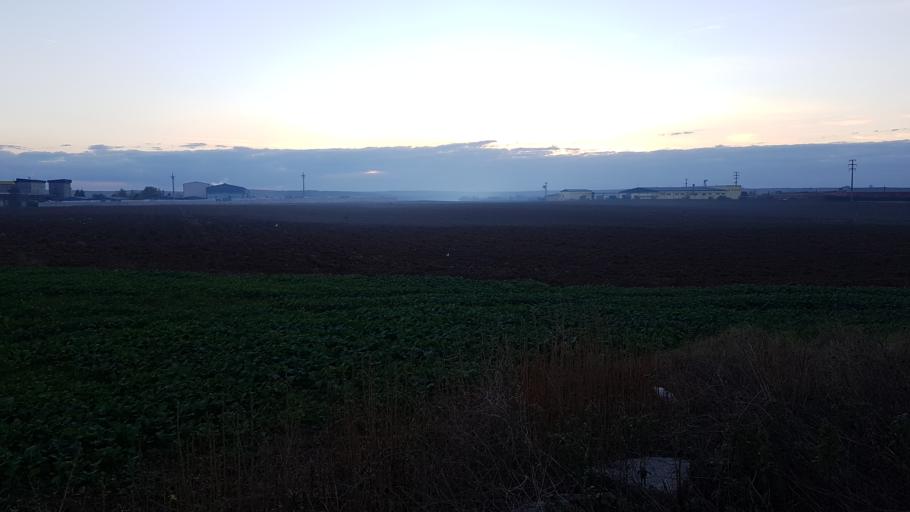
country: TR
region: Tekirdag
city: Muratli
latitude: 41.1924
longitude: 27.5106
